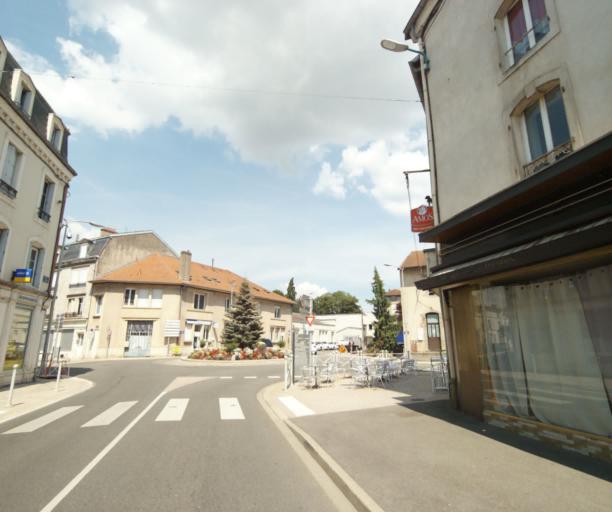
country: FR
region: Lorraine
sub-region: Departement de Meurthe-et-Moselle
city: Luneville
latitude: 48.5904
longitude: 6.4910
